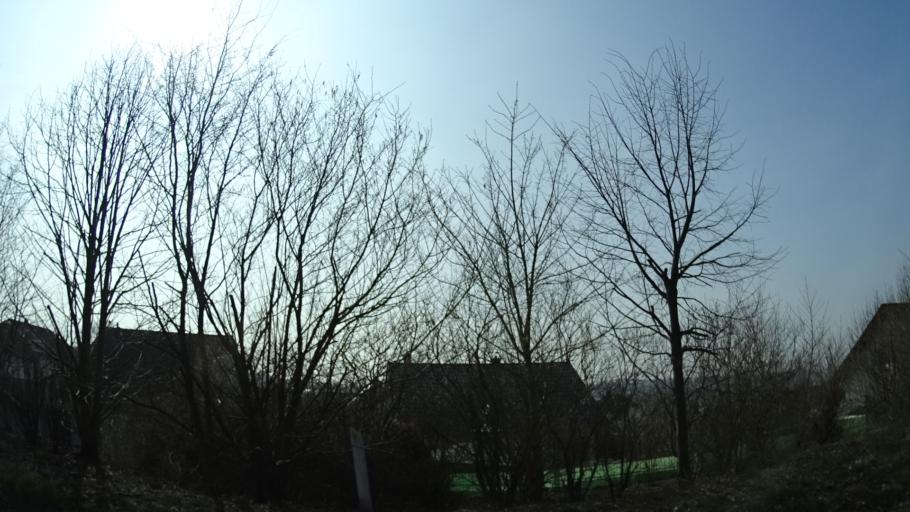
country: DE
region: Rheinland-Pfalz
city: Baumholder
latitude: 49.6105
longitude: 7.3452
